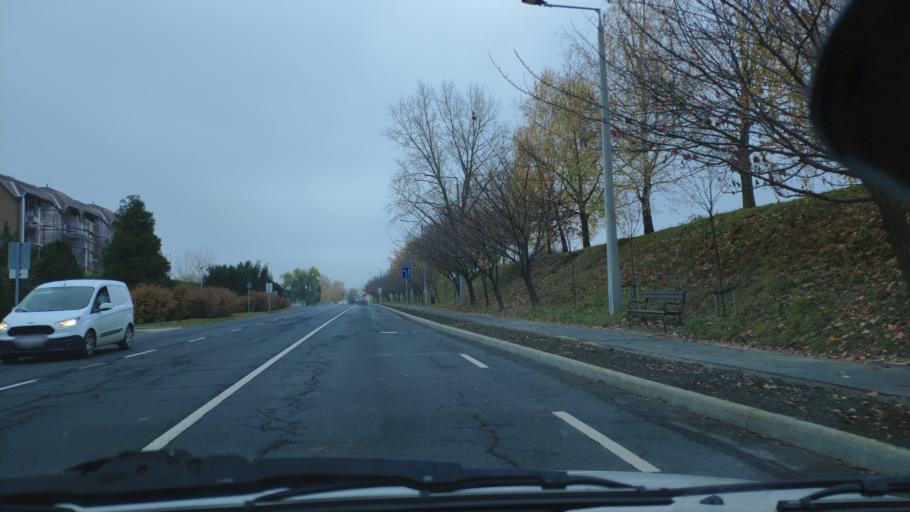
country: HU
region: Zala
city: Zalakomar
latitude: 46.5447
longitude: 17.1253
